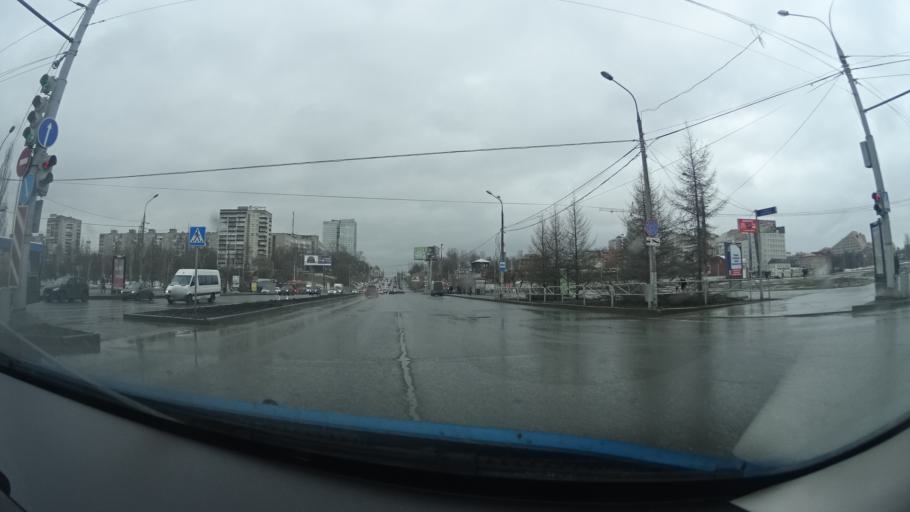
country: RU
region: Perm
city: Perm
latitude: 58.0087
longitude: 56.2278
